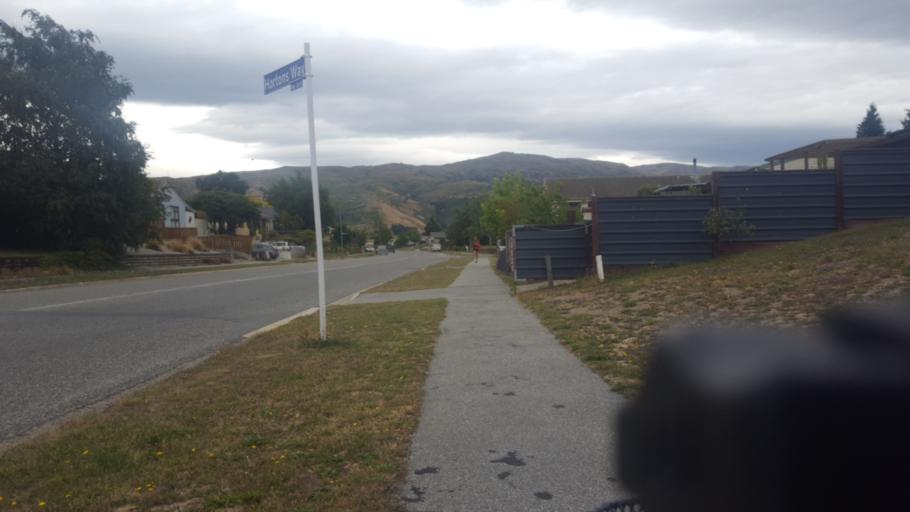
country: NZ
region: Otago
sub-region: Queenstown-Lakes District
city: Wanaka
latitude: -45.0471
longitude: 169.1847
